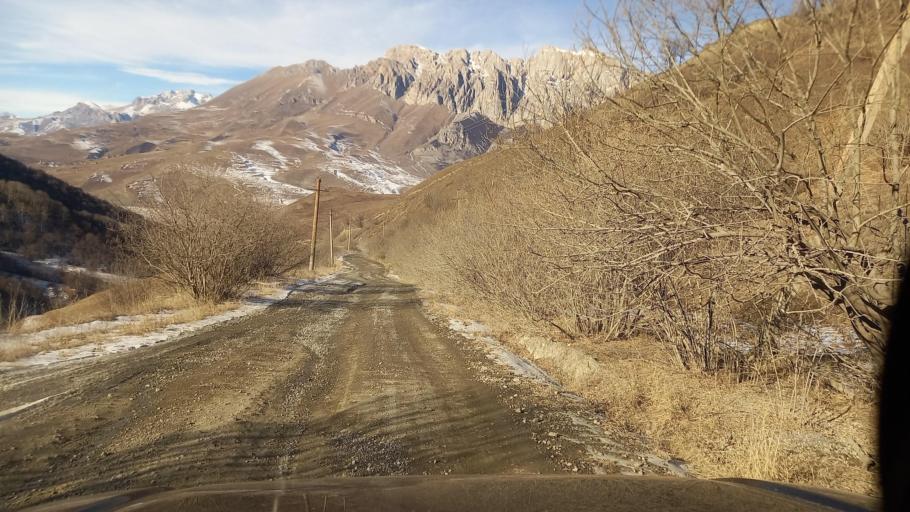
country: RU
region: North Ossetia
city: Verkhniy Fiagdon
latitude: 42.8354
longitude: 44.4719
